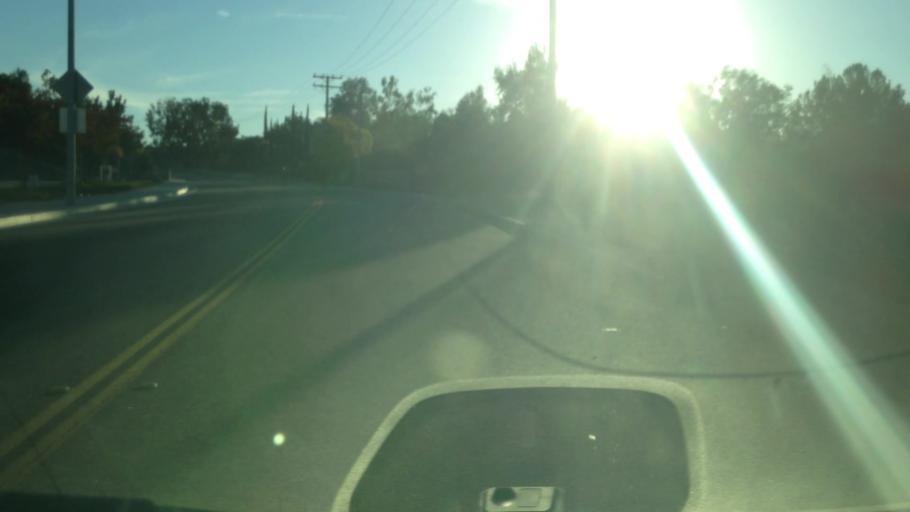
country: US
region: California
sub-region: Riverside County
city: Woodcrest
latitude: 33.8778
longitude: -117.4351
